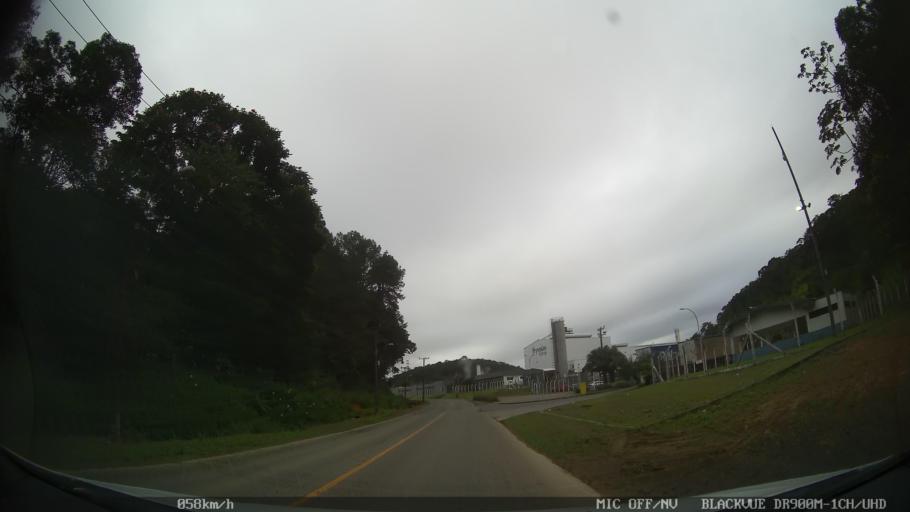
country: BR
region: Santa Catarina
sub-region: Joinville
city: Joinville
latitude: -26.2529
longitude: -48.9174
